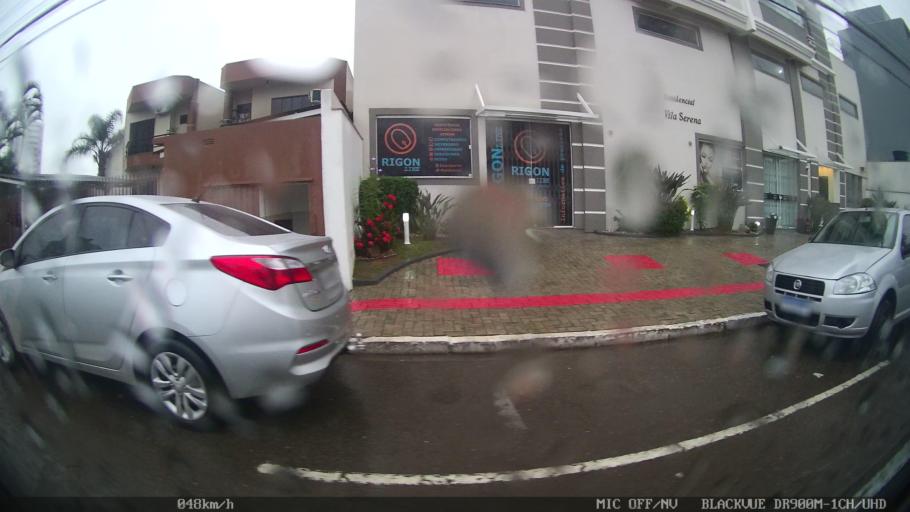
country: BR
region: Santa Catarina
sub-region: Itajai
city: Itajai
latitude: -26.9136
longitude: -48.6707
